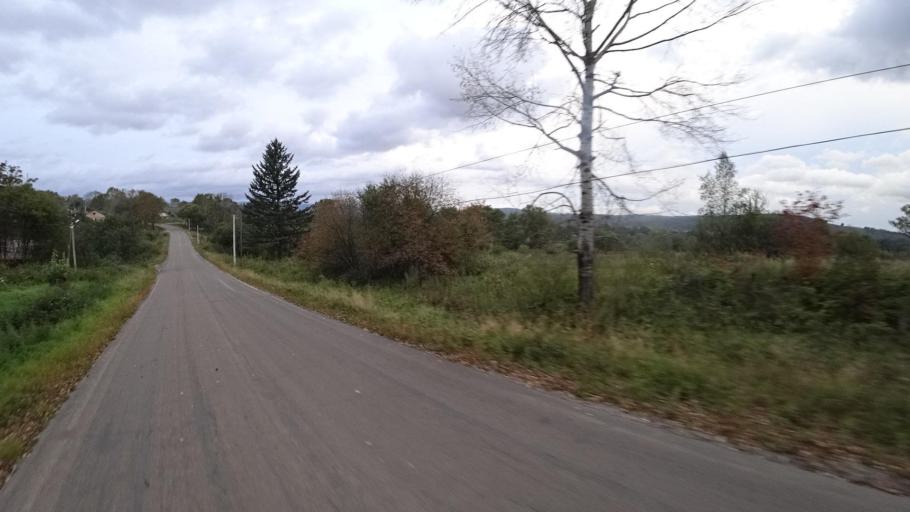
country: RU
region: Jewish Autonomous Oblast
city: Izvestkovyy
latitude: 48.9713
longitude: 131.5829
